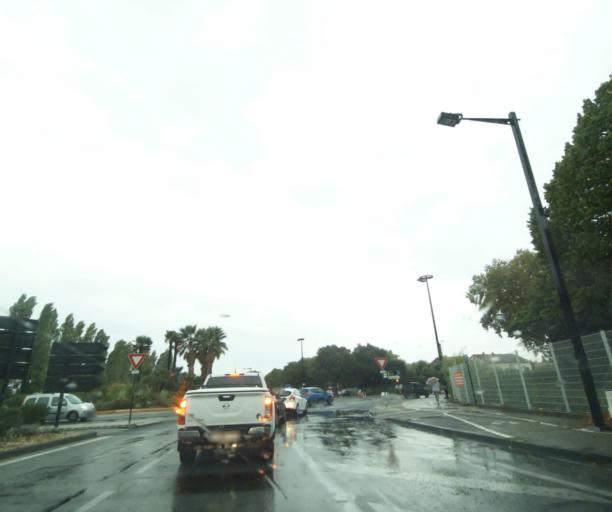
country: FR
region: Languedoc-Roussillon
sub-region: Departement du Gard
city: Nimes
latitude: 43.8374
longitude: 4.3882
